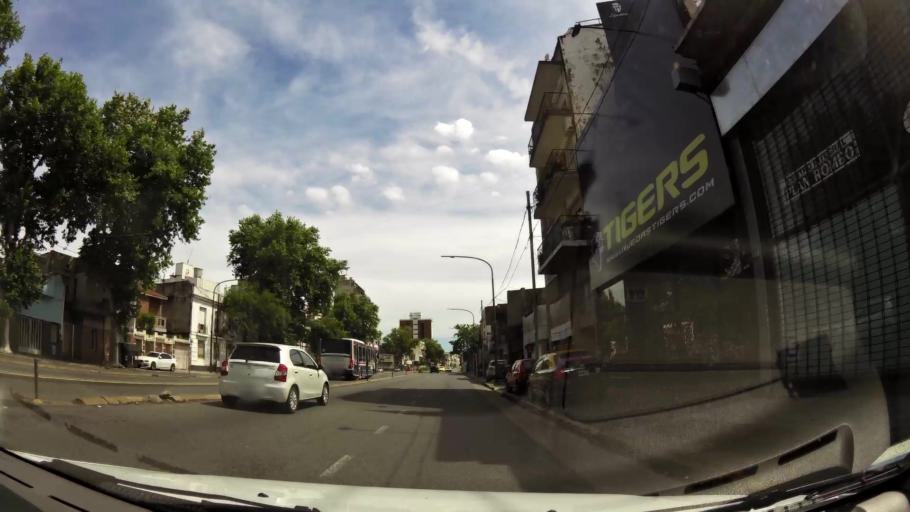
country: AR
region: Buenos Aires F.D.
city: Villa Santa Rita
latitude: -34.6210
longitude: -58.4798
